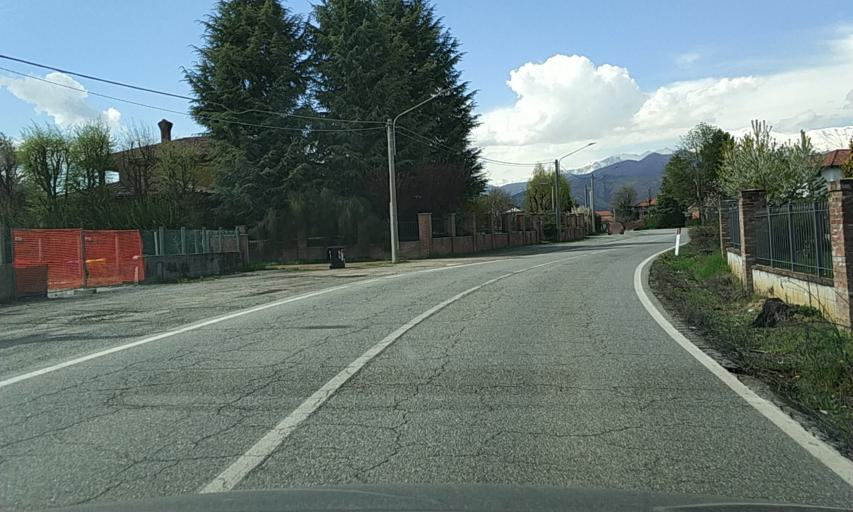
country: IT
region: Piedmont
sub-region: Provincia di Torino
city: San Carlo Canavese
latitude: 45.2517
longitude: 7.5911
